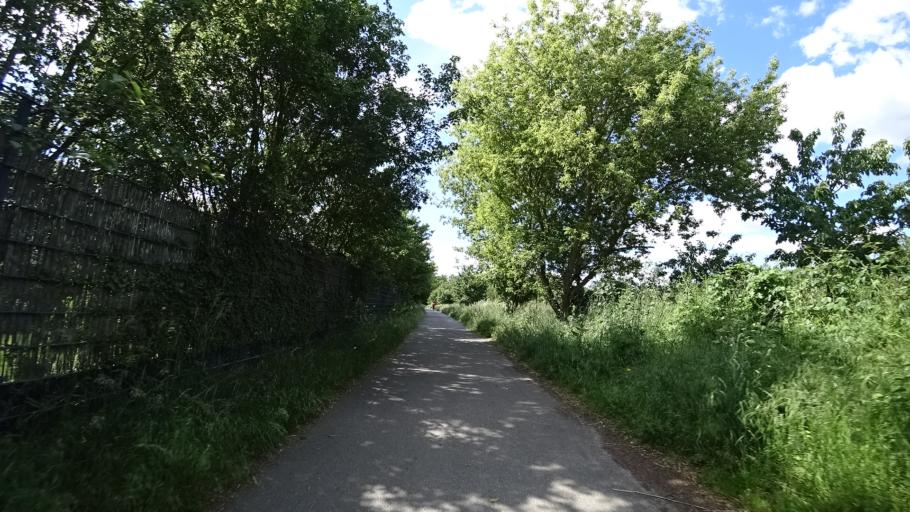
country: DE
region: Berlin
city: Lichtenrade
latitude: 52.3902
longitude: 13.3808
